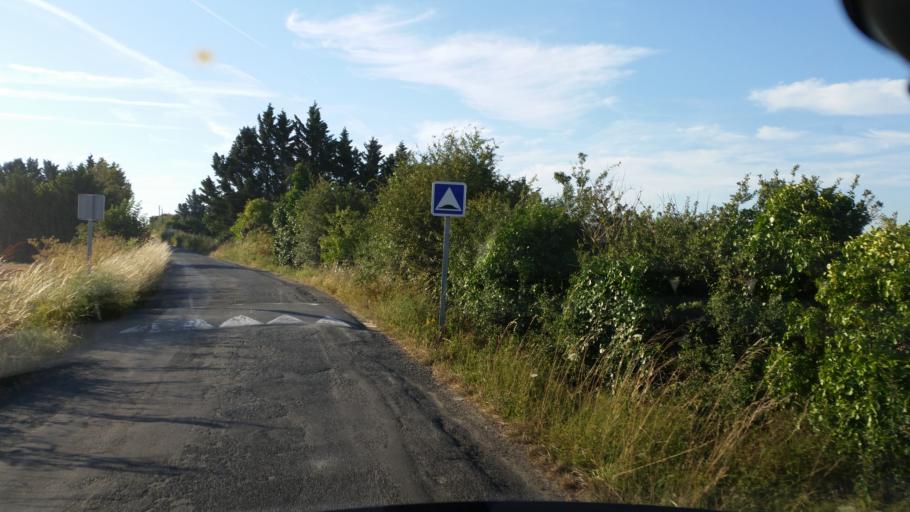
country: FR
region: Poitou-Charentes
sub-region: Departement de la Charente-Maritime
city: Marans
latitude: 46.2998
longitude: -0.9936
